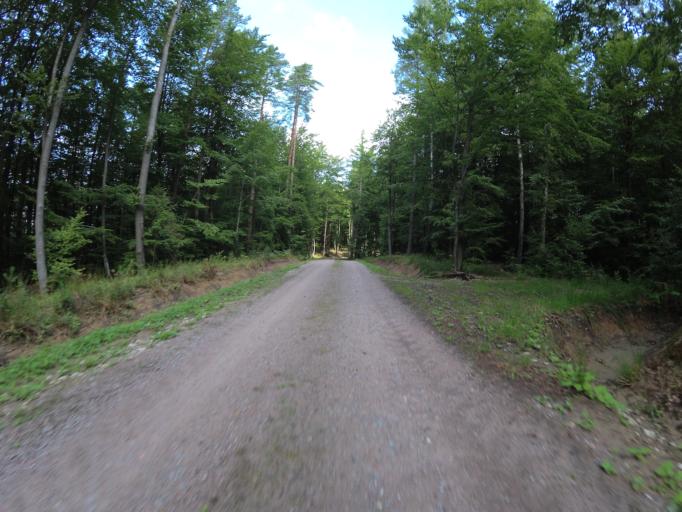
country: PL
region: Pomeranian Voivodeship
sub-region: Powiat wejherowski
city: Bojano
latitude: 54.5164
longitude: 18.4248
